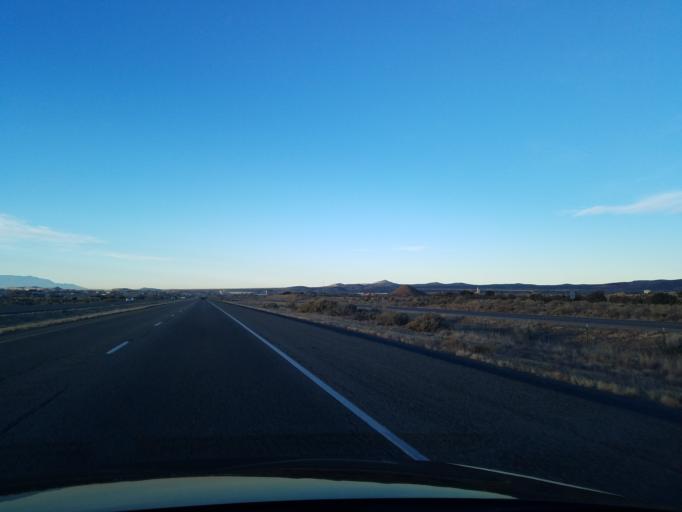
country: US
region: New Mexico
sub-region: Santa Fe County
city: Agua Fria
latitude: 35.6451
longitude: -106.0589
